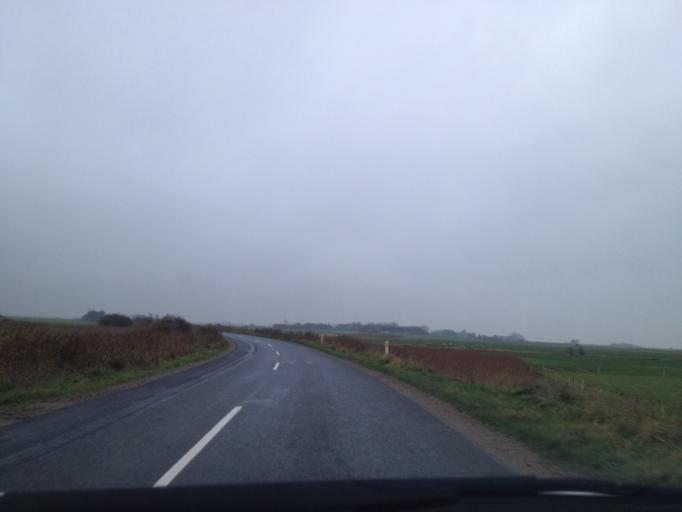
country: DK
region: South Denmark
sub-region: Tonder Kommune
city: Sherrebek
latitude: 55.1139
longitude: 8.7333
